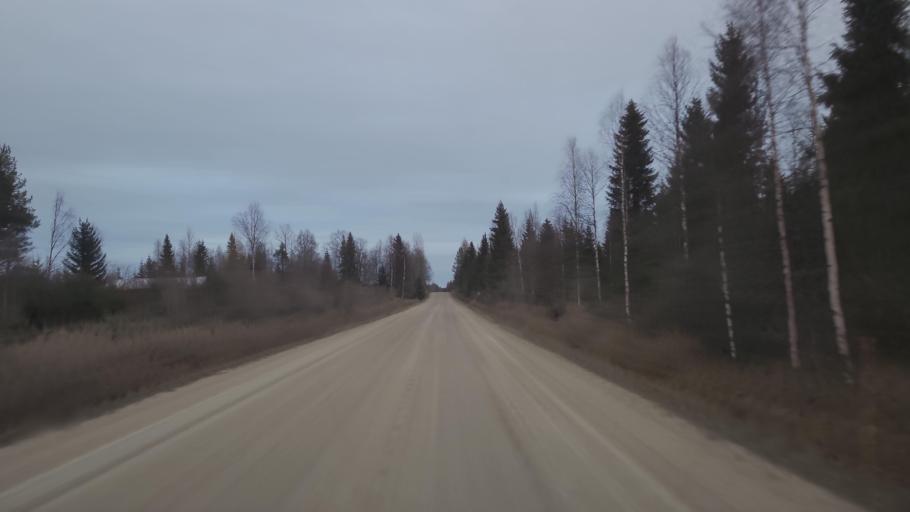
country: FI
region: Lapland
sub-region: Kemi-Tornio
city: Tervola
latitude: 66.0727
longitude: 24.8605
